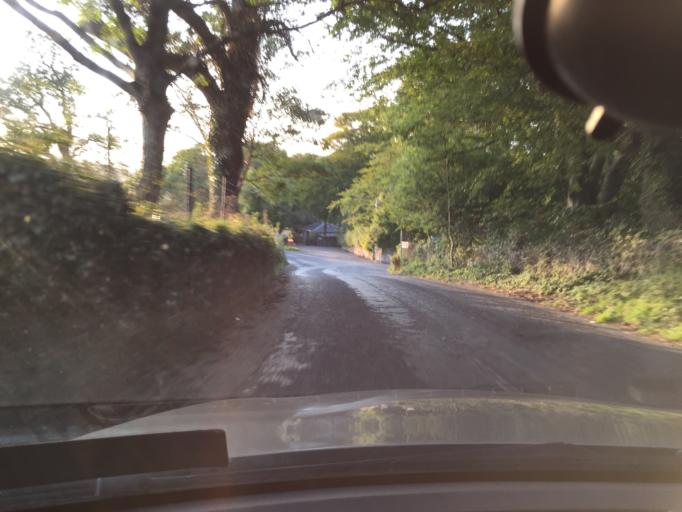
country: IE
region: Leinster
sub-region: Wicklow
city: Enniskerry
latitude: 53.1688
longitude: -6.1795
